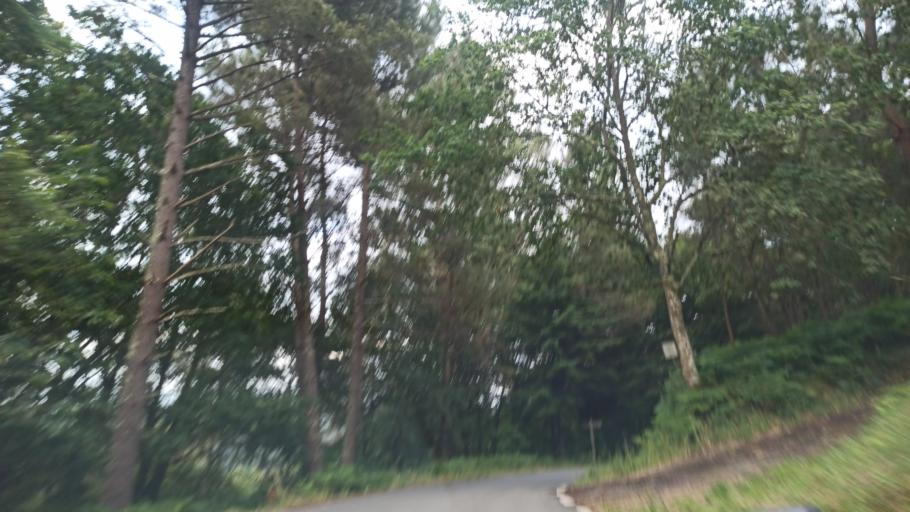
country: ES
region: Galicia
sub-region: Provincia da Coruna
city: Santiso
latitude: 42.8262
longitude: -8.1404
